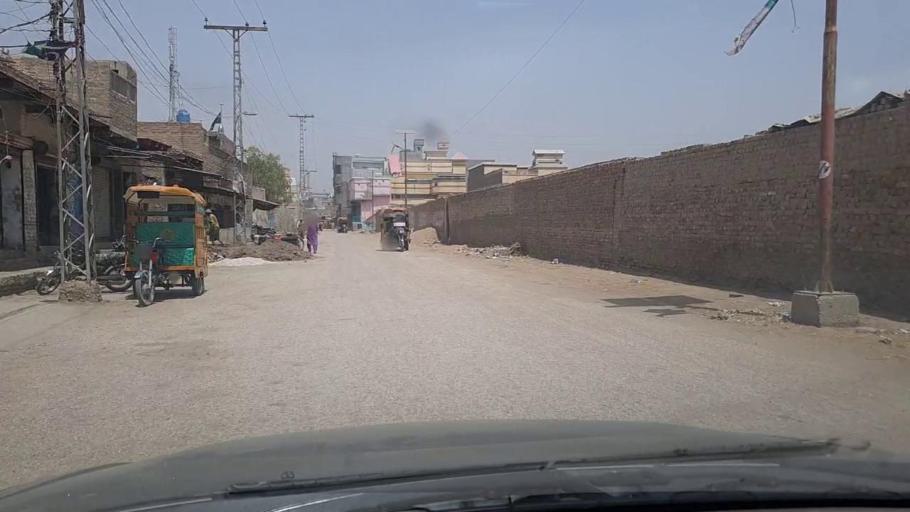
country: PK
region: Sindh
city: Ratodero
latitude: 27.8000
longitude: 68.2871
